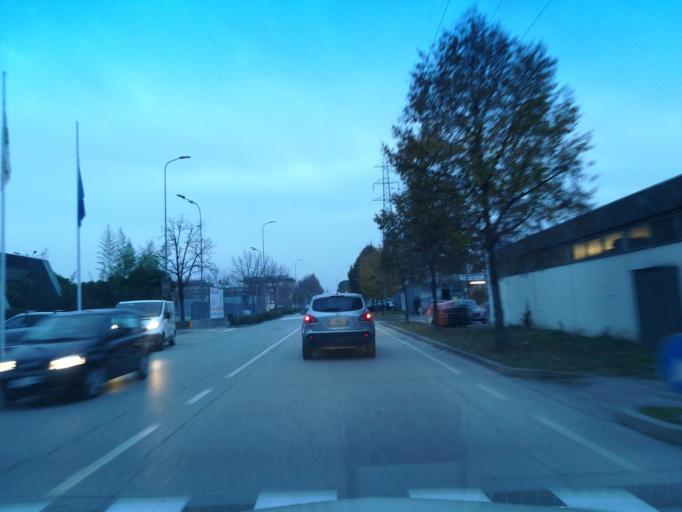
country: IT
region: Emilia-Romagna
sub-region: Provincia di Ravenna
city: Faenza
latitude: 44.2951
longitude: 11.8647
